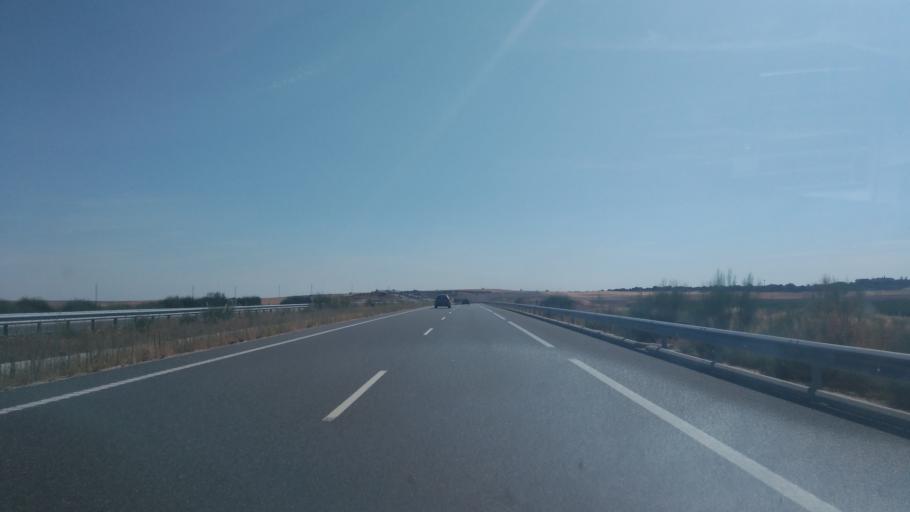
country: ES
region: Castille and Leon
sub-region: Provincia de Salamanca
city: Villar de Gallimazo
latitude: 40.9270
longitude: -5.2734
